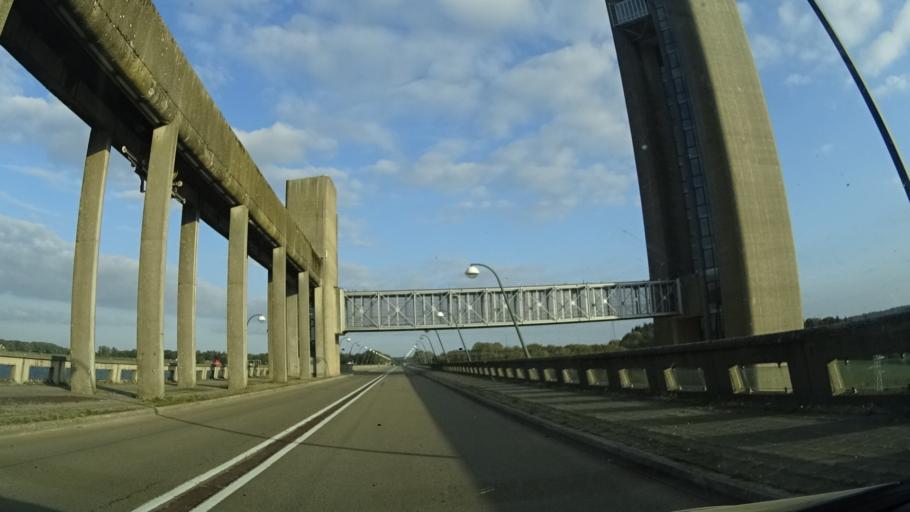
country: BE
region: Wallonia
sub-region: Province de Namur
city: Cerfontaine
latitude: 50.1882
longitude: 4.3864
